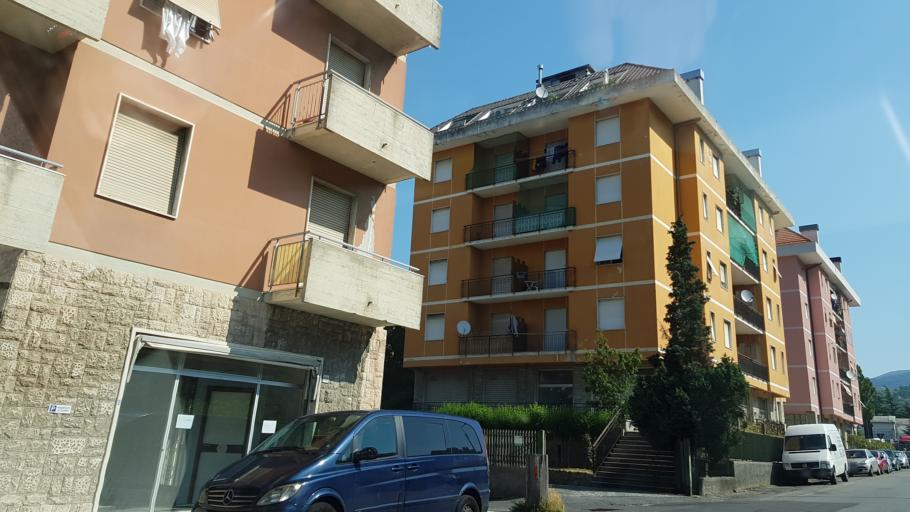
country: IT
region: Liguria
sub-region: Provincia di Genova
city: Pedemonte
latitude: 44.4997
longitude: 8.9240
